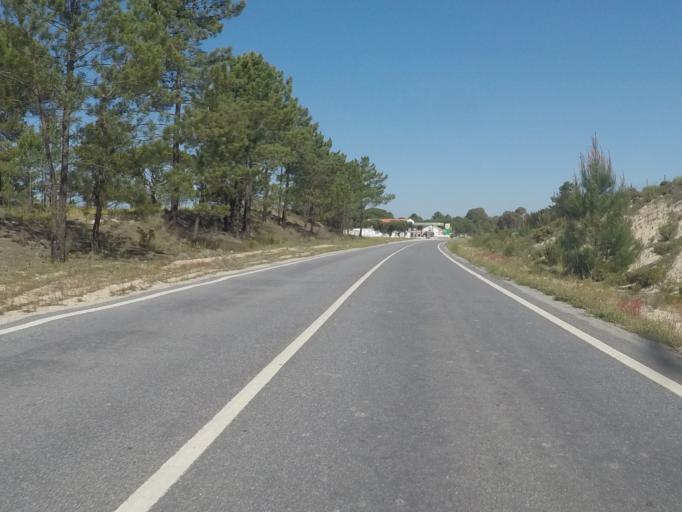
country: PT
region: Setubal
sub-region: Grandola
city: Grandola
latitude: 38.3081
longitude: -8.7412
